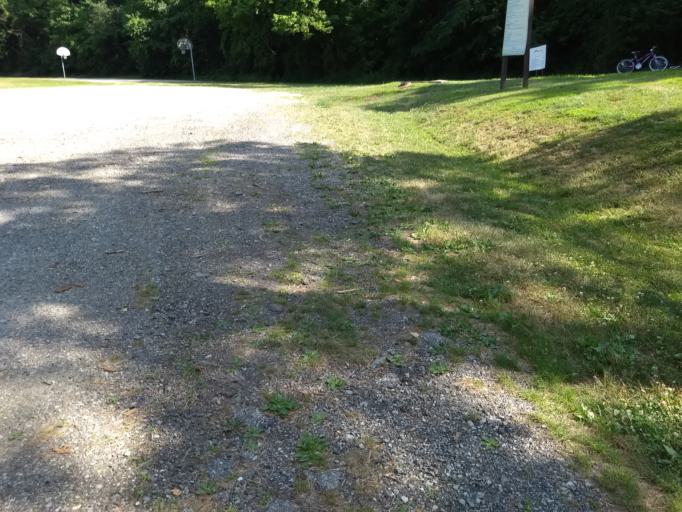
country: US
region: Pennsylvania
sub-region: Westmoreland County
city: Irwin
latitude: 40.3322
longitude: -79.7219
